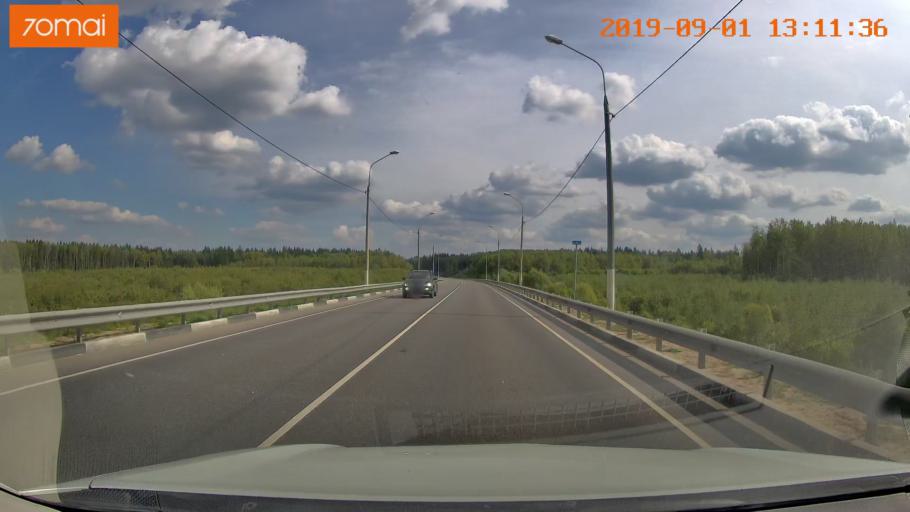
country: RU
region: Kaluga
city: Maloyaroslavets
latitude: 54.9784
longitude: 36.4382
